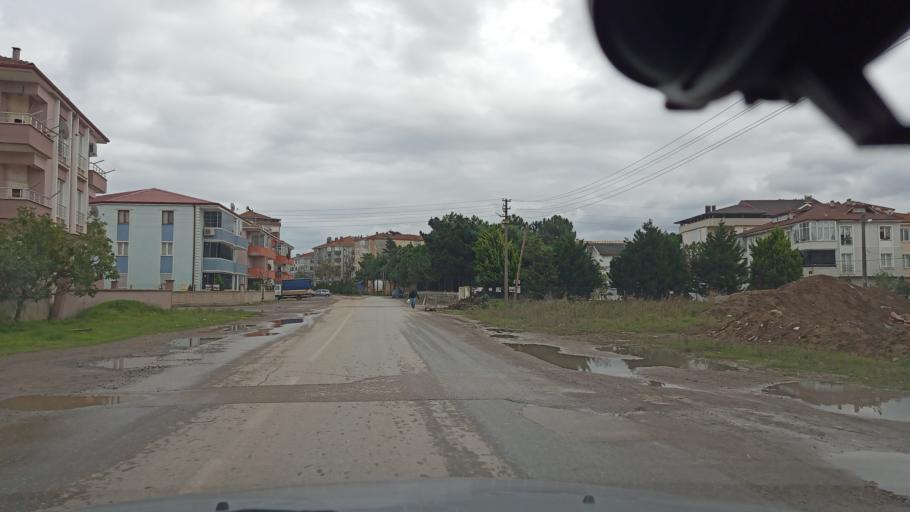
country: TR
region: Sakarya
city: Karasu
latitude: 41.1080
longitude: 30.6899
